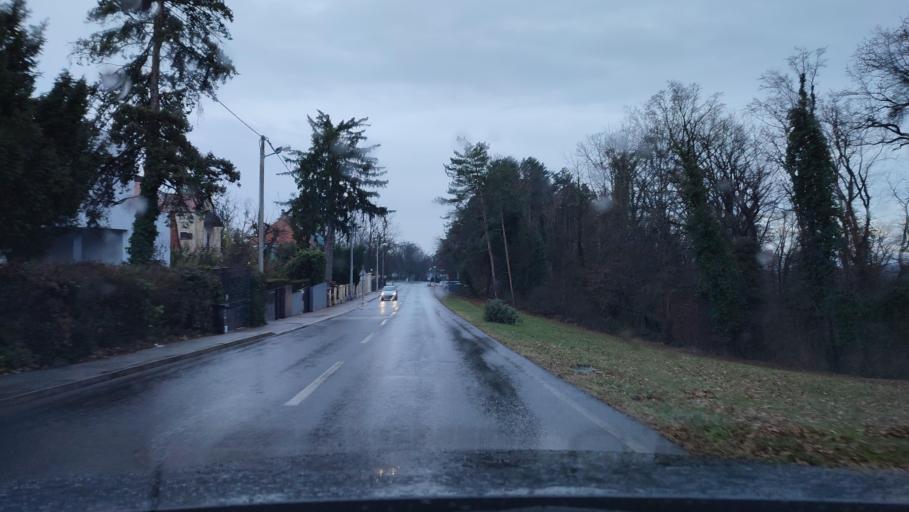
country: HR
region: Grad Zagreb
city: Zagreb
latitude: 45.8375
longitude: 15.9709
